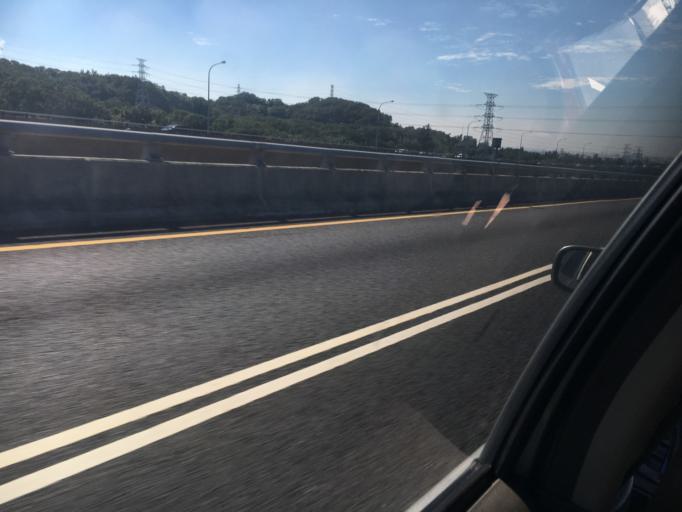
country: TW
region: Taiwan
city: Taoyuan City
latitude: 25.0460
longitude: 121.3140
